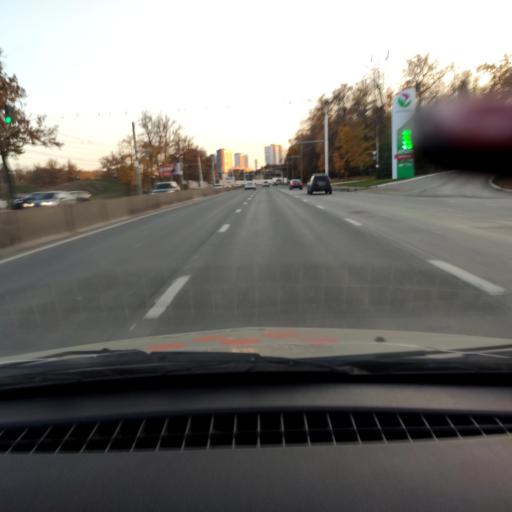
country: RU
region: Bashkortostan
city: Ufa
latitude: 54.7317
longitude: 56.0250
